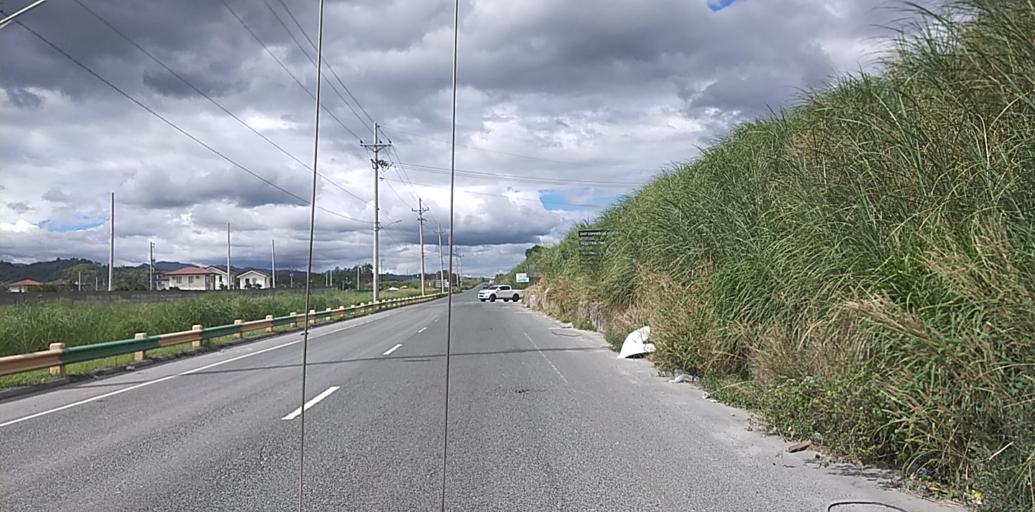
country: PH
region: Central Luzon
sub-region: Province of Pampanga
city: Dolores
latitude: 15.1144
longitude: 120.5157
